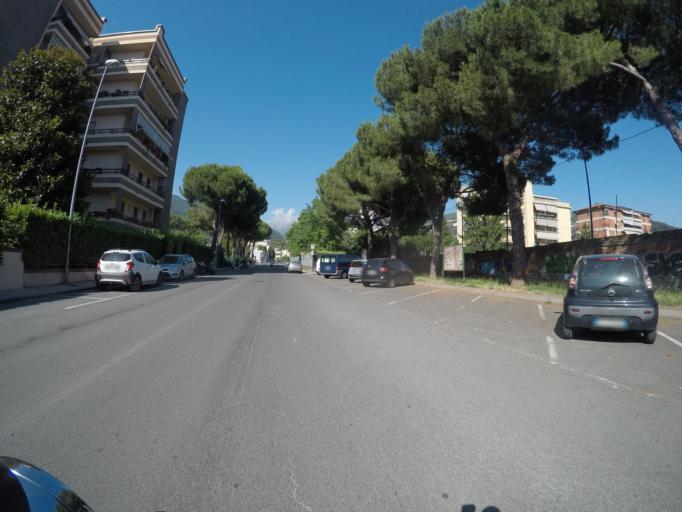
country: IT
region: Tuscany
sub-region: Provincia di Massa-Carrara
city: Massa
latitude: 44.0335
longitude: 10.1333
